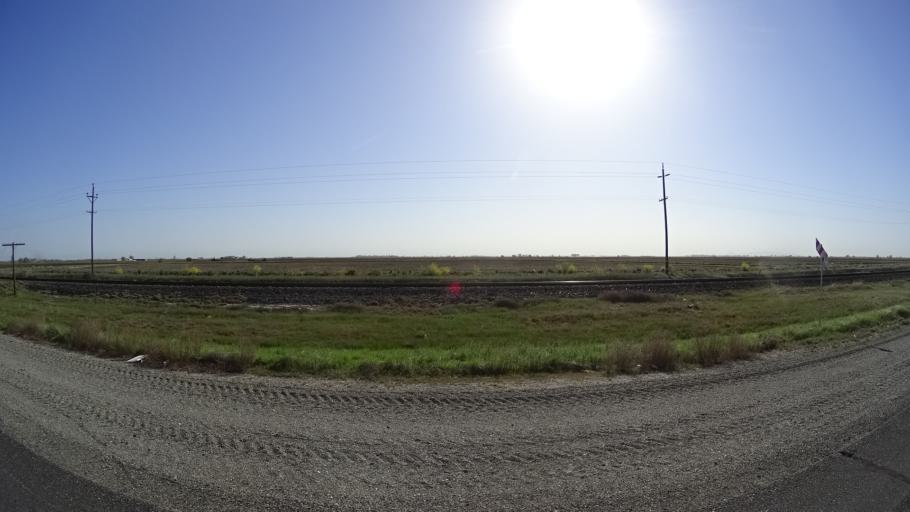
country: US
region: California
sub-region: Glenn County
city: Willows
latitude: 39.4875
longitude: -122.1932
